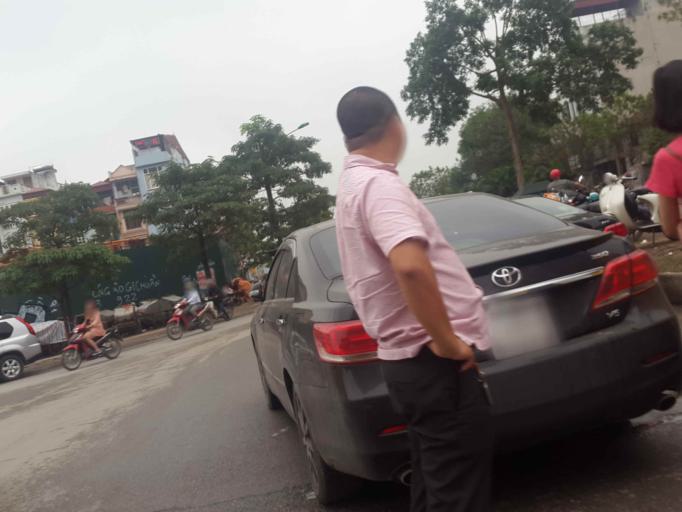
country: VN
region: Ha Noi
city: Cau Giay
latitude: 21.0434
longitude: 105.8167
